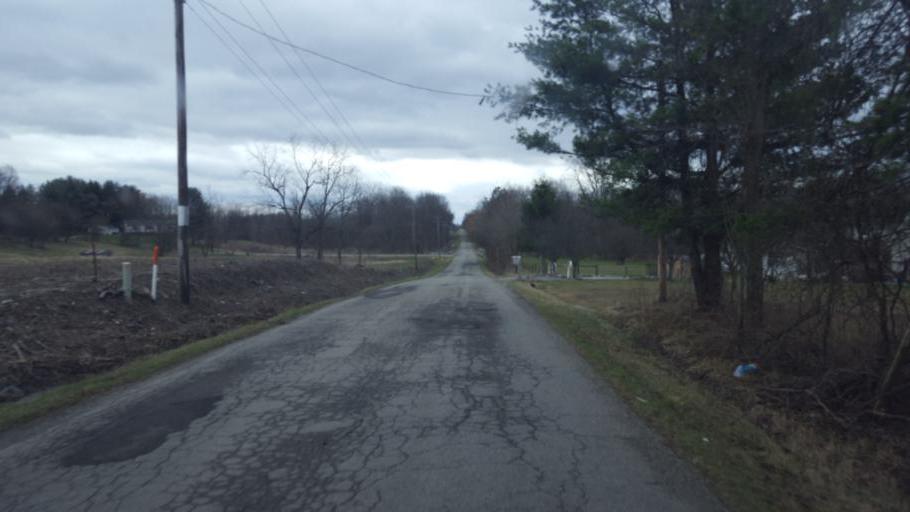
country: US
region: Ohio
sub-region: Knox County
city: Centerburg
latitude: 40.4333
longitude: -82.6814
